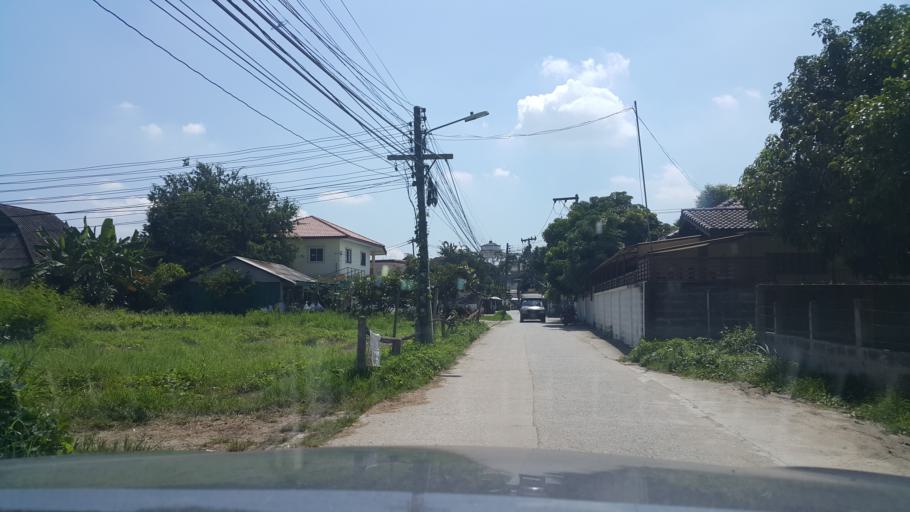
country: TH
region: Chiang Mai
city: Chiang Mai
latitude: 18.8480
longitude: 98.9772
